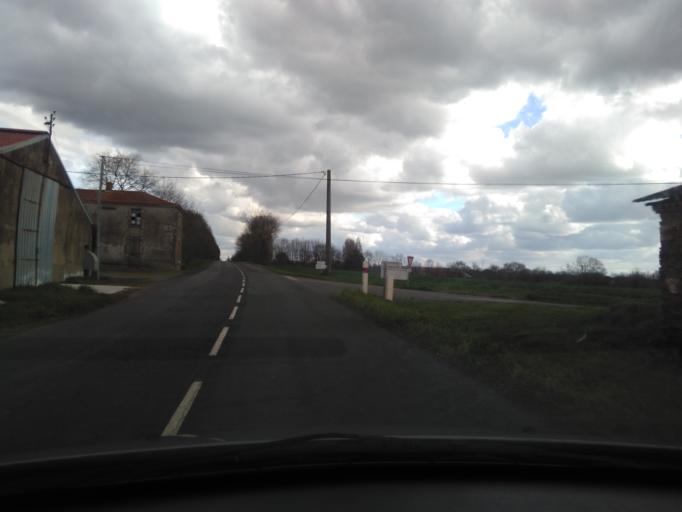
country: FR
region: Pays de la Loire
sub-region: Departement de la Vendee
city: Les Essarts
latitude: 46.7484
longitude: -1.2068
